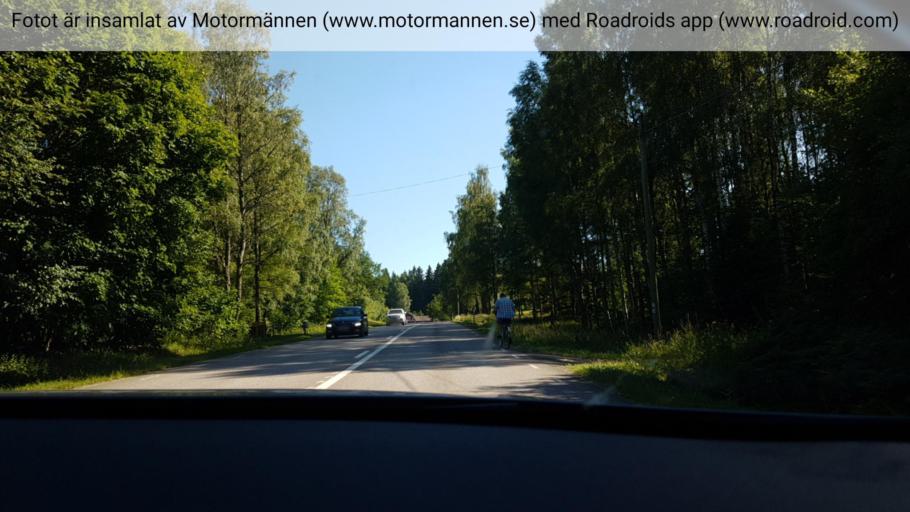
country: SE
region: Vaestra Goetaland
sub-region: Skara Kommun
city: Skara
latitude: 58.3212
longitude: 13.4340
